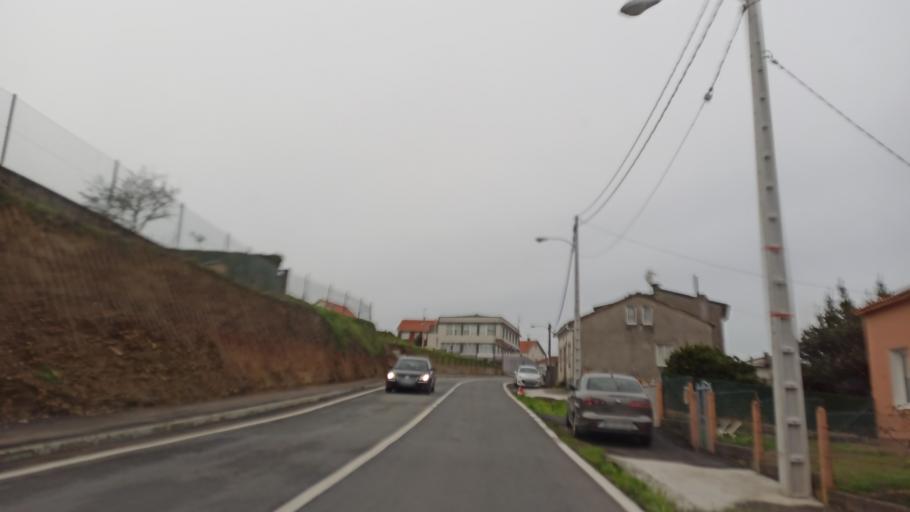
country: ES
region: Galicia
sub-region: Provincia da Coruna
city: Oleiros
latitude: 43.3893
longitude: -8.3058
